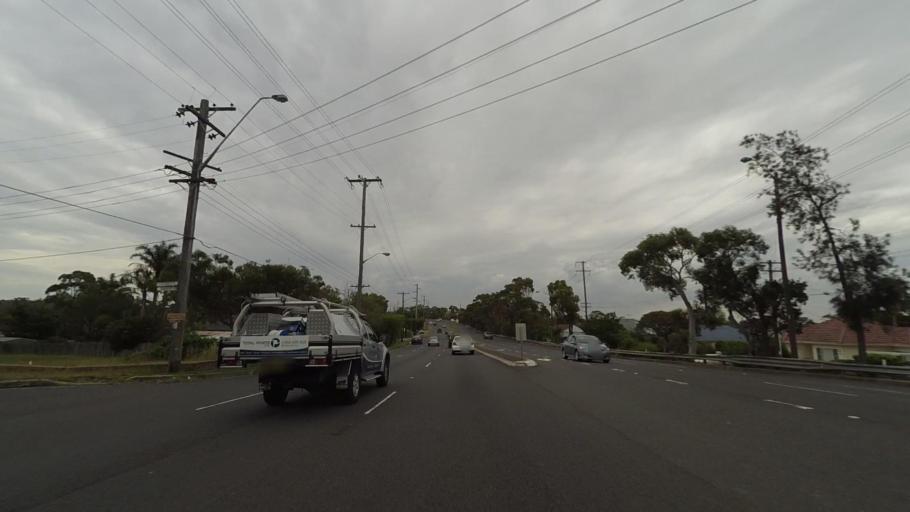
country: AU
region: New South Wales
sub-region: Sutherland Shire
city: Engadine
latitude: -34.0600
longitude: 151.0261
